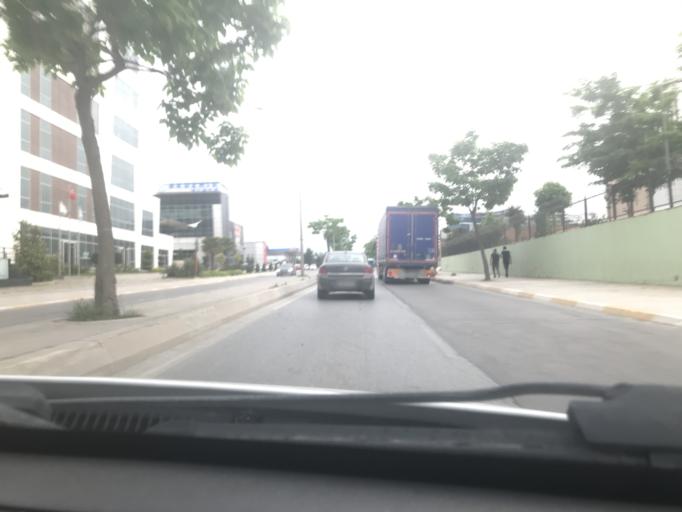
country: TR
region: Istanbul
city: Sultanbeyli
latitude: 40.9279
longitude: 29.3194
